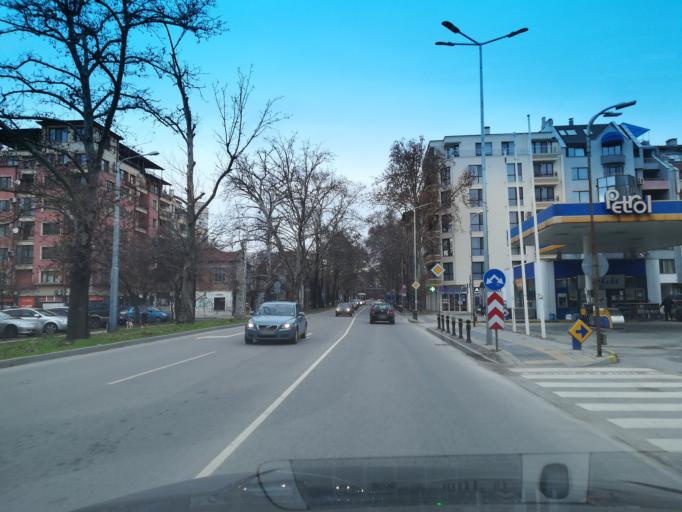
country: BG
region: Plovdiv
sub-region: Obshtina Plovdiv
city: Plovdiv
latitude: 42.1440
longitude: 24.7323
